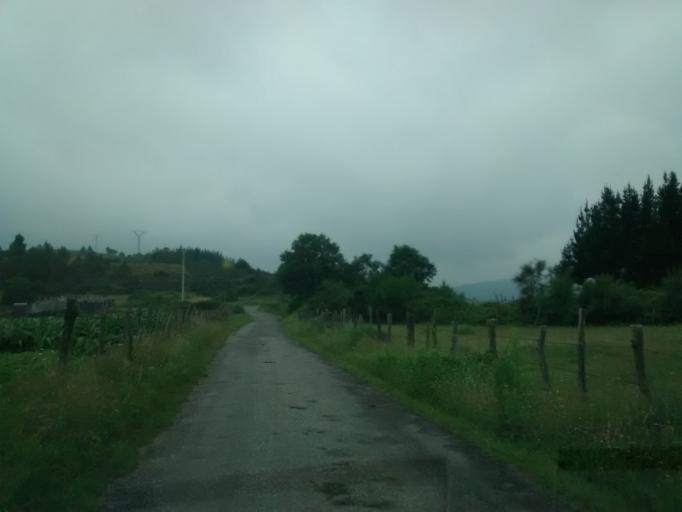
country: ES
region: Galicia
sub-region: Provincia de Ourense
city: Castro Caldelas
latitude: 42.4061
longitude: -7.4012
